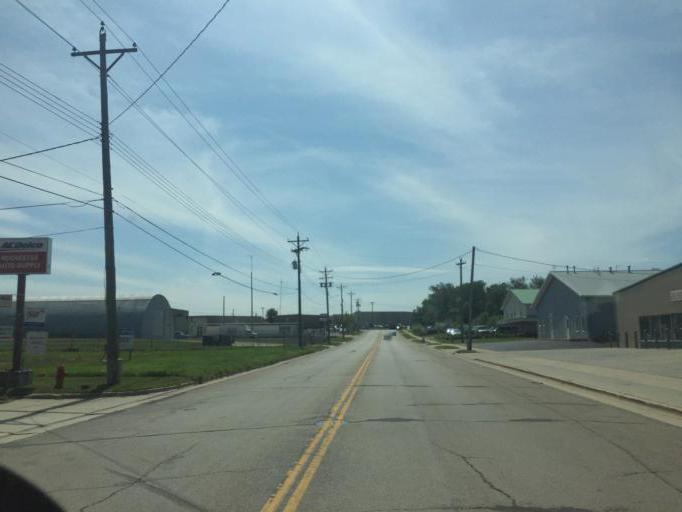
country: US
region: Minnesota
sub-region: Olmsted County
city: Rochester
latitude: 43.9951
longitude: -92.4587
